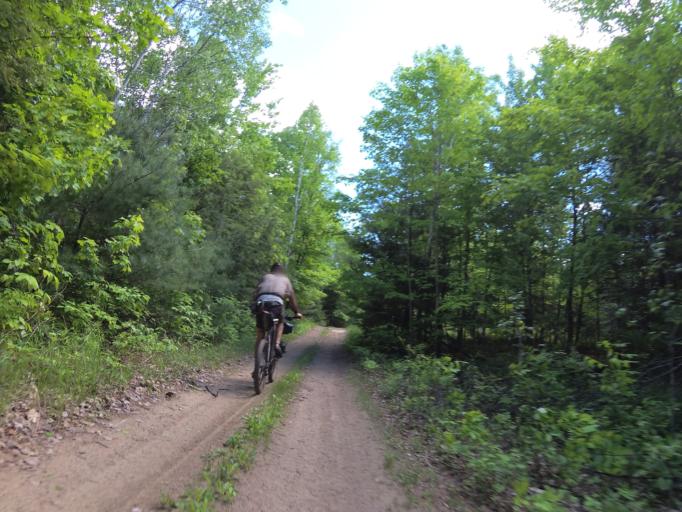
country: CA
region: Ontario
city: Renfrew
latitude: 45.0534
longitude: -76.8389
